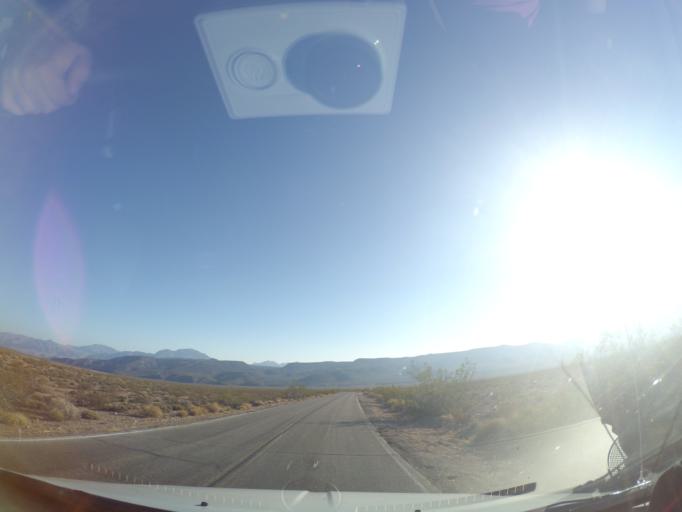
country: US
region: Nevada
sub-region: Nye County
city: Beatty
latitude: 36.2472
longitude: -116.6817
